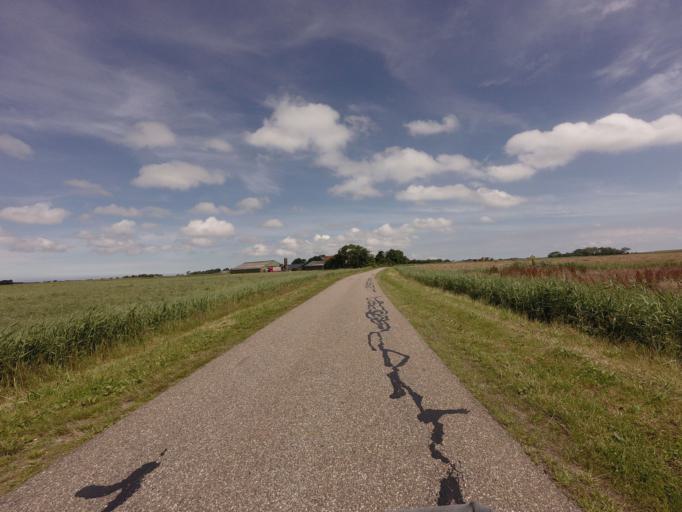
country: NL
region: North Holland
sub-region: Gemeente Texel
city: Den Burg
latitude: 53.0634
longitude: 4.8507
